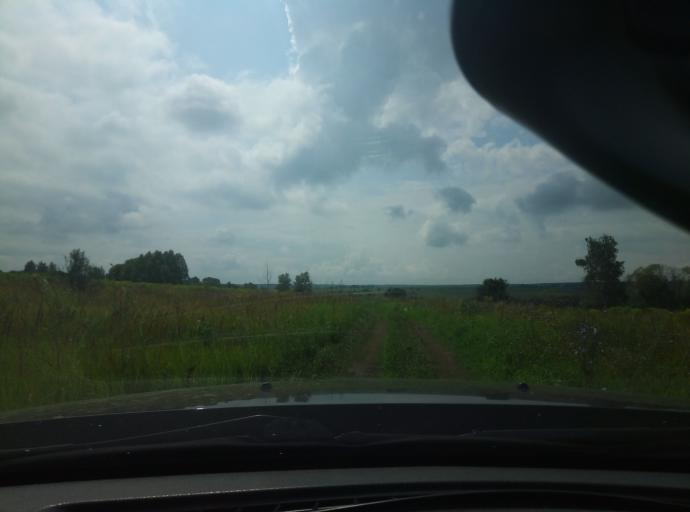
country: RU
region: Tula
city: Shvartsevskiy
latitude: 54.0825
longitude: 38.0213
